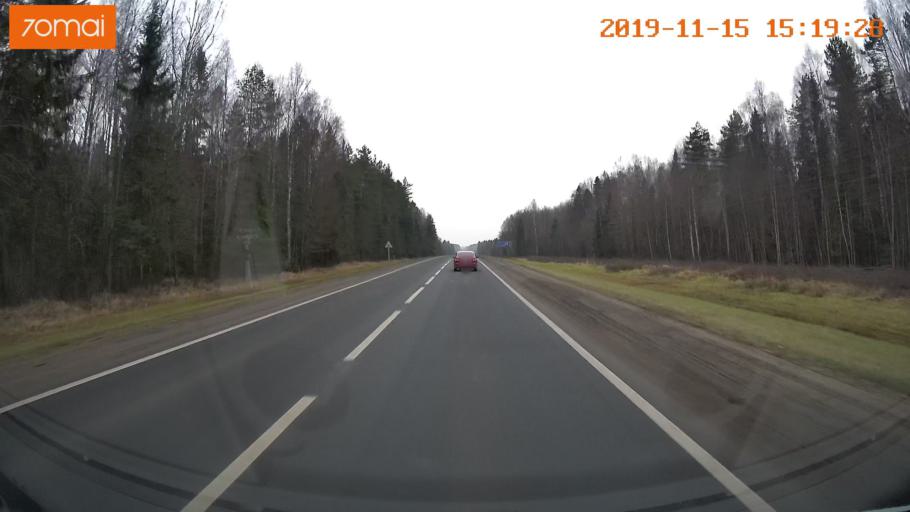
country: RU
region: Jaroslavl
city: Danilov
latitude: 58.2339
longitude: 40.1771
